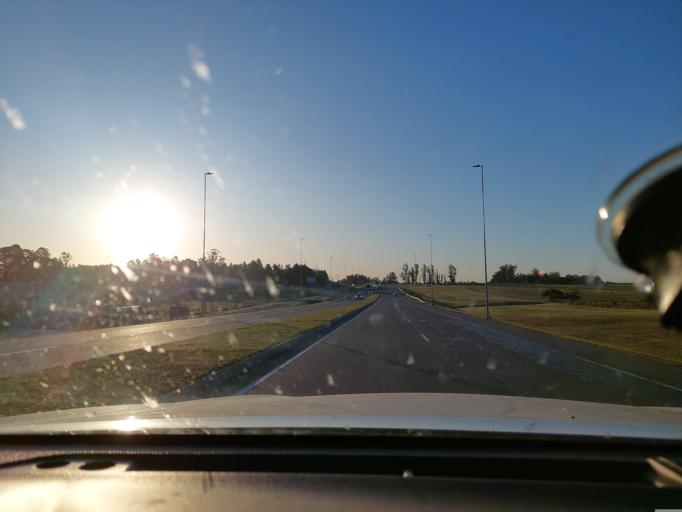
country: UY
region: Canelones
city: Empalme Olmos
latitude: -34.7006
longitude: -55.9114
